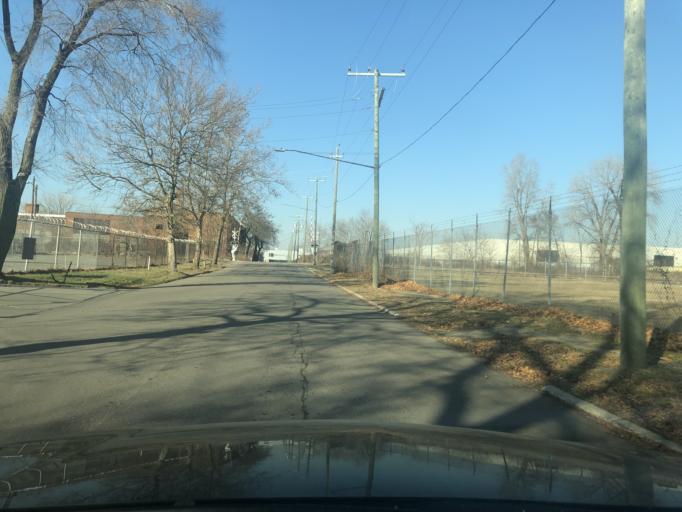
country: US
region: Michigan
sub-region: Wayne County
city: Detroit
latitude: 42.3078
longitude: -83.0908
